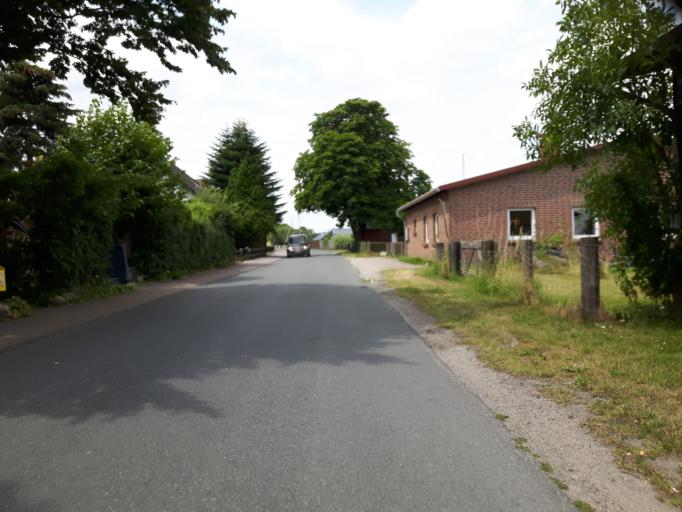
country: DE
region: Lower Saxony
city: Varel
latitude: 53.4078
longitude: 8.1793
